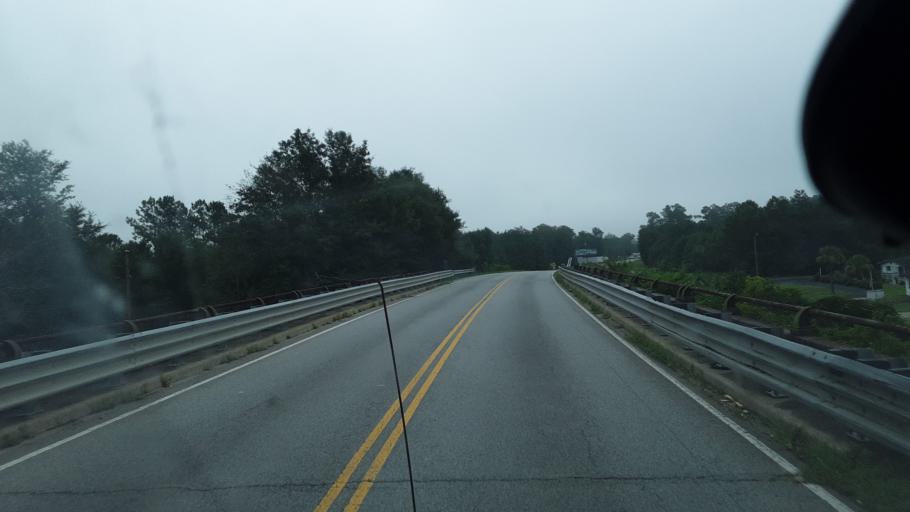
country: US
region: South Carolina
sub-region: Florence County
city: Johnsonville
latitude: 33.9144
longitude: -79.4138
